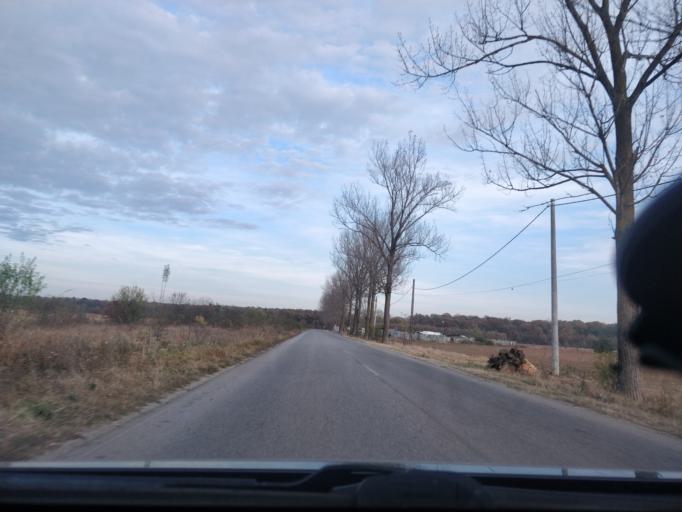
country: RO
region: Giurgiu
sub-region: Comuna Crevedia Mare
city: Crevedia Mare
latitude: 44.4317
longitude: 25.6534
